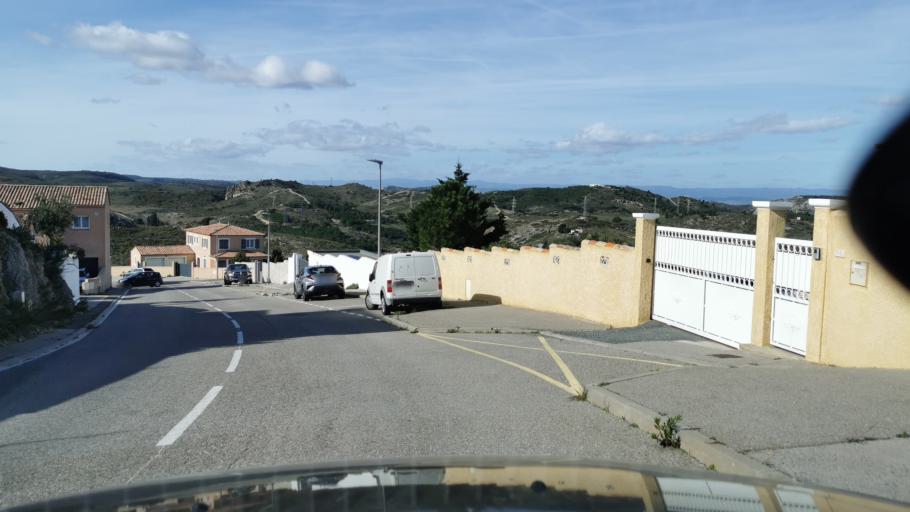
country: FR
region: Languedoc-Roussillon
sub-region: Departement de l'Aude
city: Narbonne
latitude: 43.1651
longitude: 2.9681
